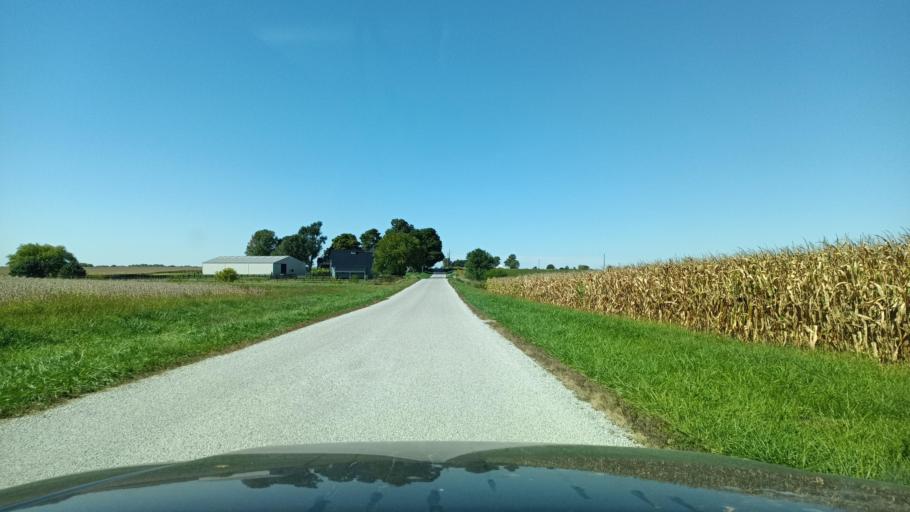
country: US
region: Illinois
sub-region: Champaign County
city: Mahomet
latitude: 40.0984
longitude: -88.4410
